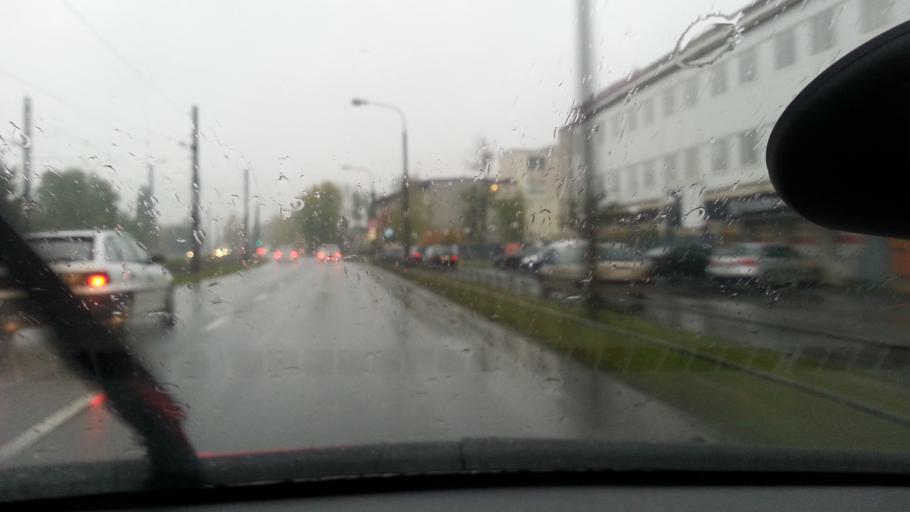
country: PL
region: Masovian Voivodeship
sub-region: Warszawa
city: Praga Polnoc
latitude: 52.2774
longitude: 21.0282
